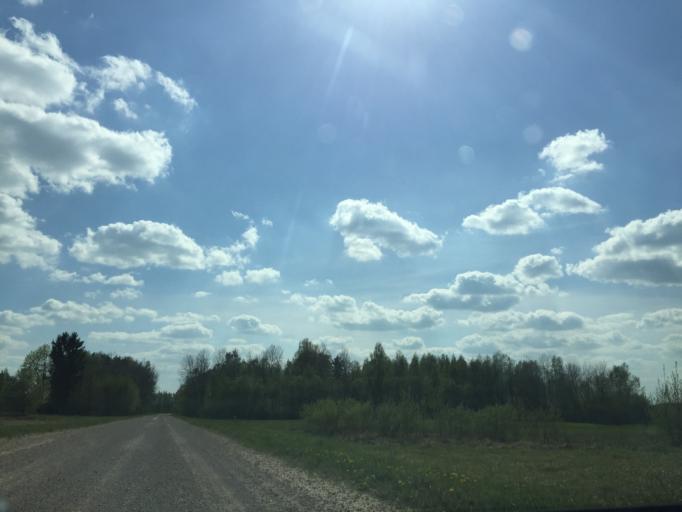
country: LV
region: Vecumnieki
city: Vecumnieki
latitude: 56.4267
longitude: 24.4982
